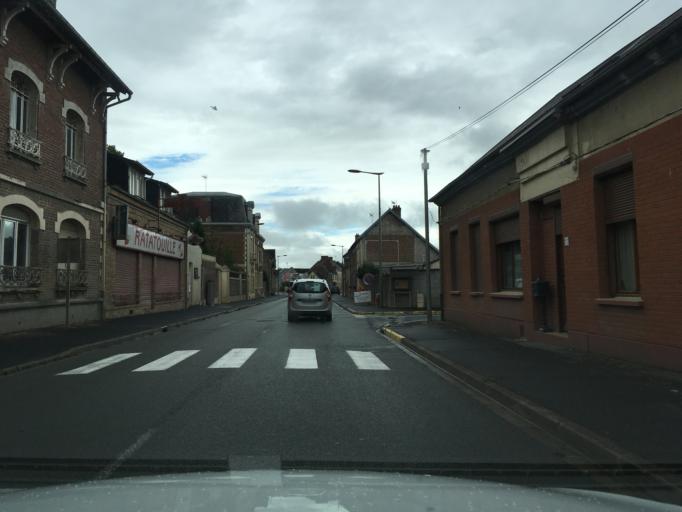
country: FR
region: Picardie
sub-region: Departement de l'Aisne
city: Origny-Sainte-Benoite
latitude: 49.8420
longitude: 3.4977
